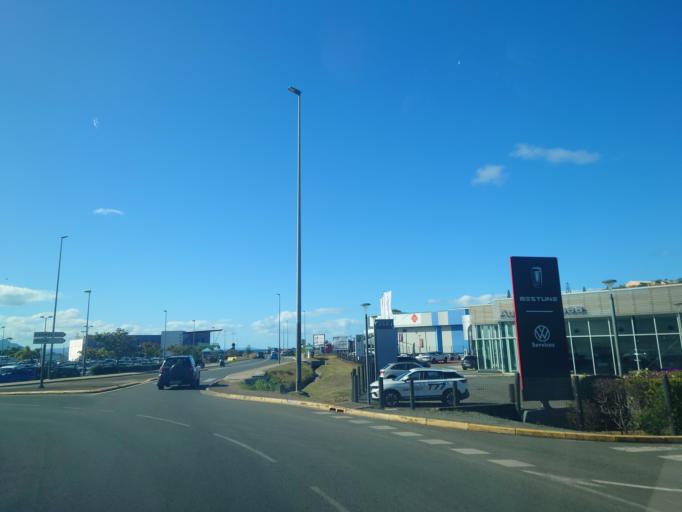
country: NC
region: South Province
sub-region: Noumea
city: Noumea
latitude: -22.2605
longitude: 166.4695
